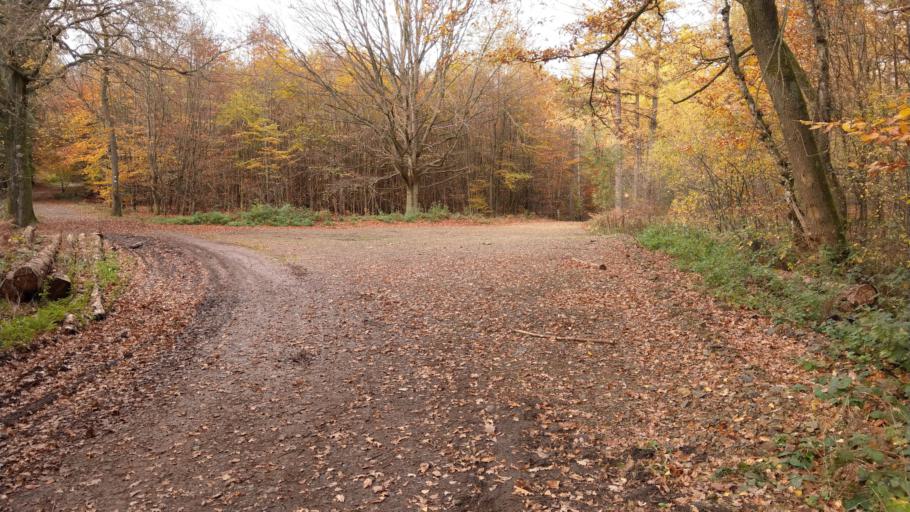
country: BE
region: Wallonia
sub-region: Province de Liege
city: La Calamine
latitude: 50.7336
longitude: 6.0206
